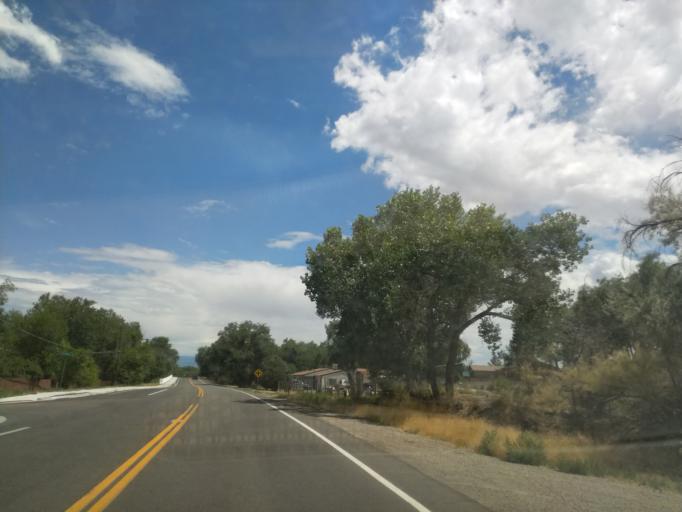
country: US
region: Colorado
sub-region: Mesa County
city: Redlands
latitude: 39.0762
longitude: -108.6306
